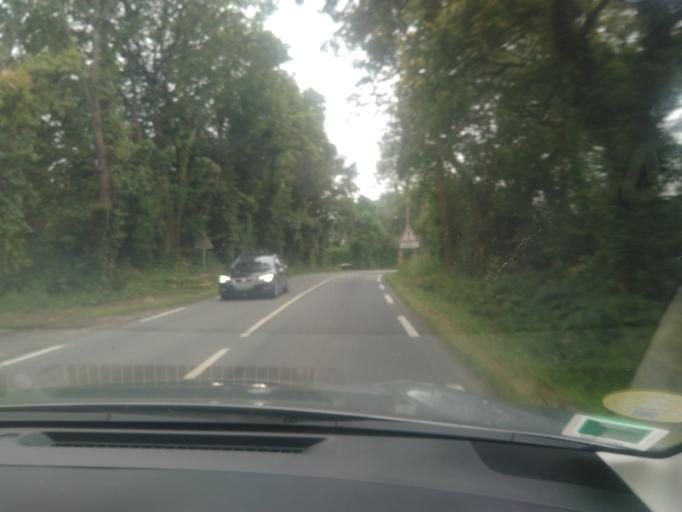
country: FR
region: Pays de la Loire
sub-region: Departement de la Loire-Atlantique
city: Saint-Andre-des-Eaux
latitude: 47.2929
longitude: -2.2778
